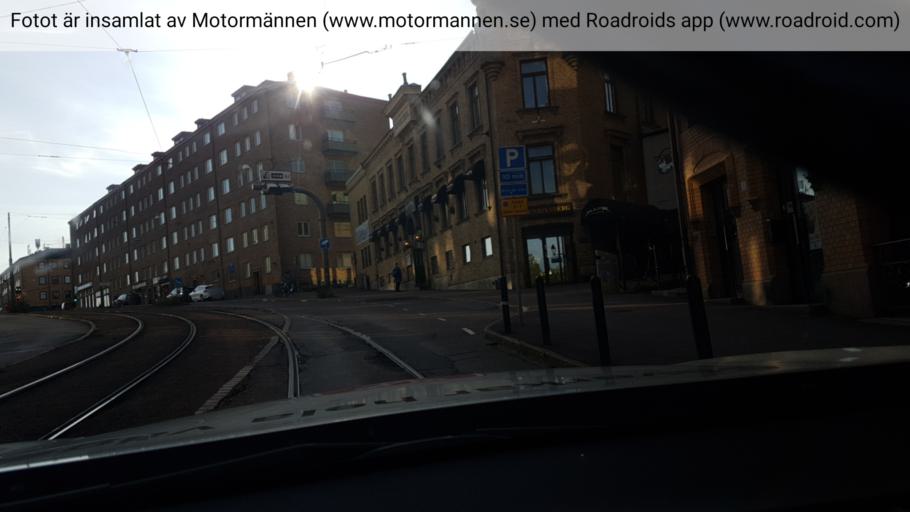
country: SE
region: Vaestra Goetaland
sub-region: Goteborg
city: Majorna
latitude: 57.6995
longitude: 11.9372
